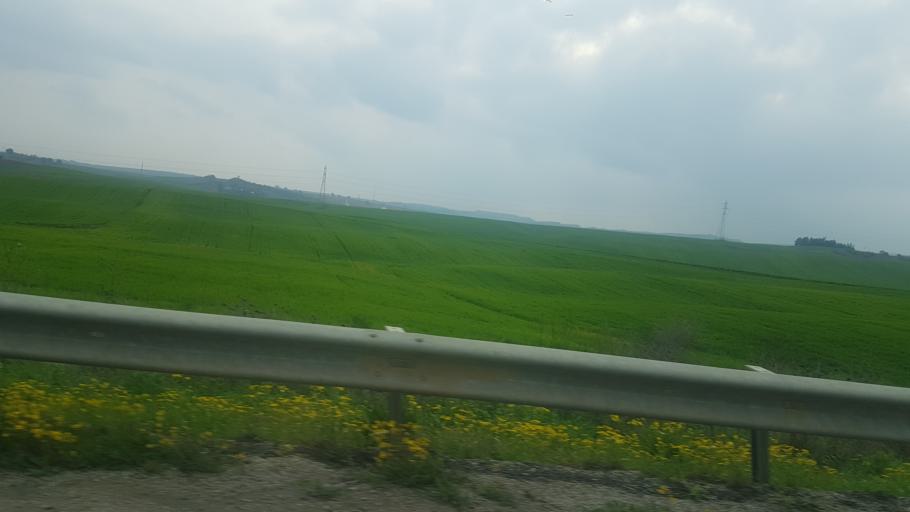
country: TR
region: Mersin
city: Yenice
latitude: 37.0711
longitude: 35.1714
